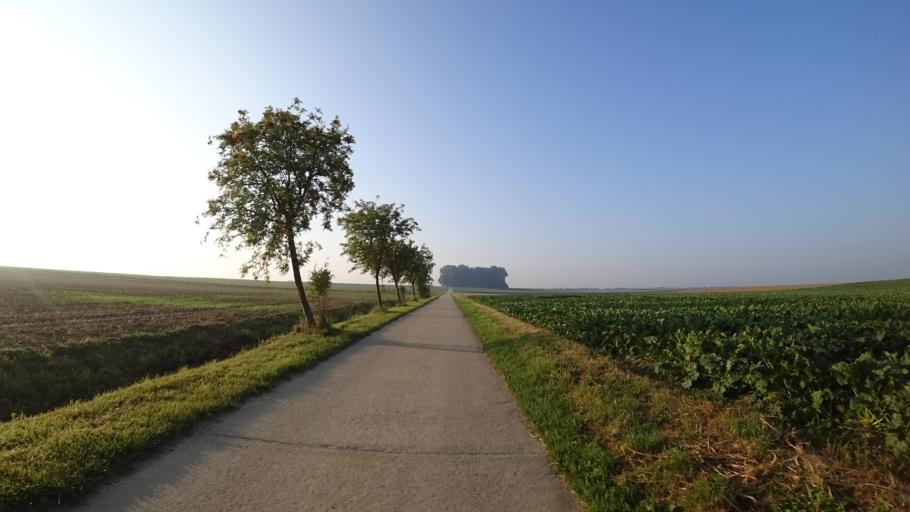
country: BE
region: Wallonia
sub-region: Province du Brabant Wallon
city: Walhain-Saint-Paul
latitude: 50.6246
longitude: 4.6776
